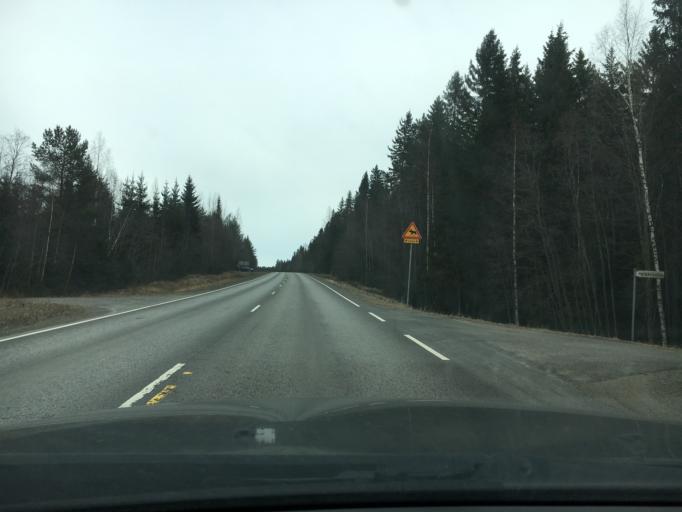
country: FI
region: Central Finland
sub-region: AEaenekoski
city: Konnevesi
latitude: 62.5957
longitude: 26.2006
